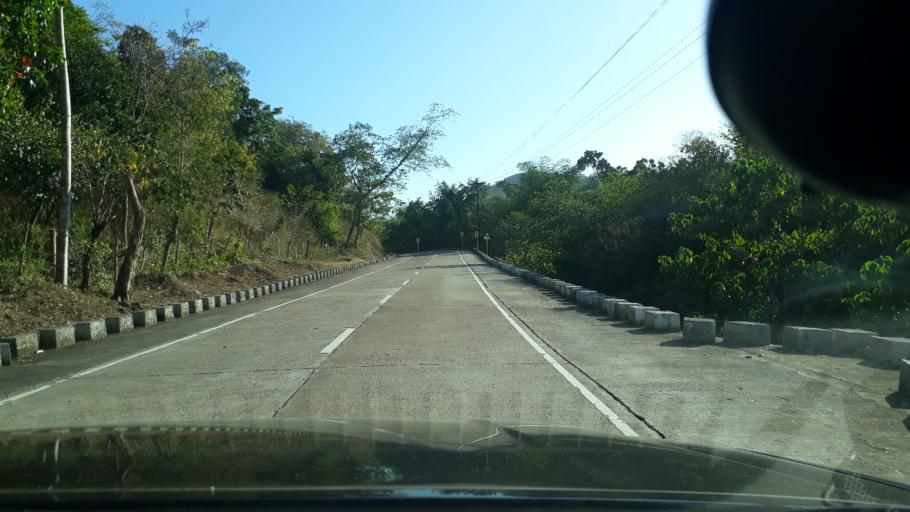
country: PH
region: Mimaropa
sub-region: Province of Palawan
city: Coron
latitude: 12.0445
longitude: 120.1560
